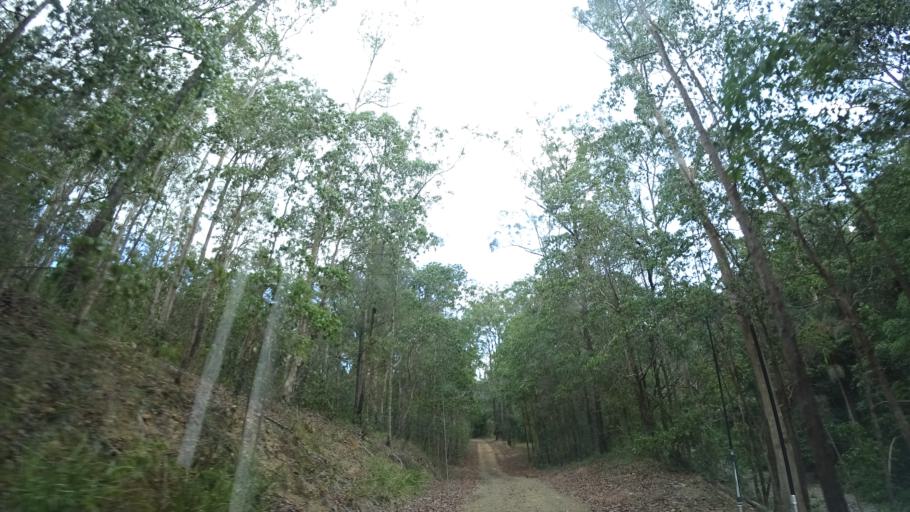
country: AU
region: Queensland
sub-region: Moreton Bay
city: Highvale
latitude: -27.3508
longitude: 152.7260
